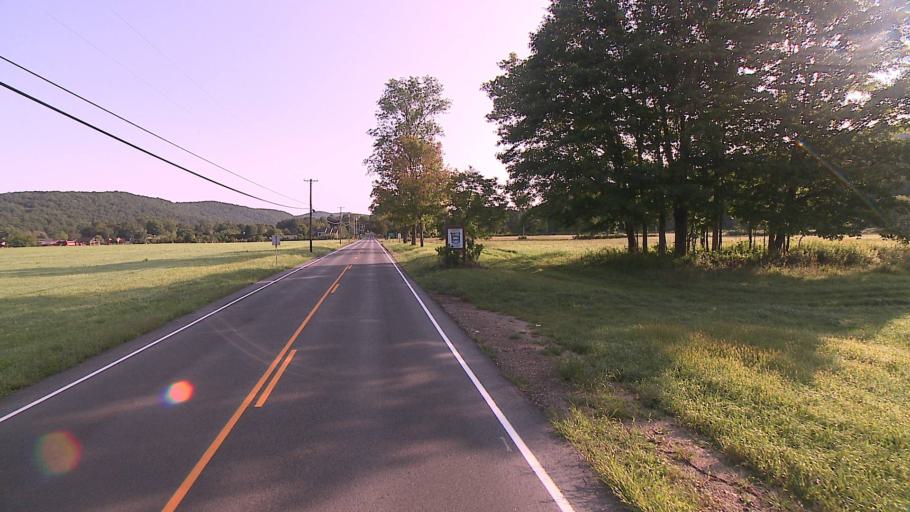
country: US
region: Connecticut
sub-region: Litchfield County
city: Kent
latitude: 41.7191
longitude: -73.4807
